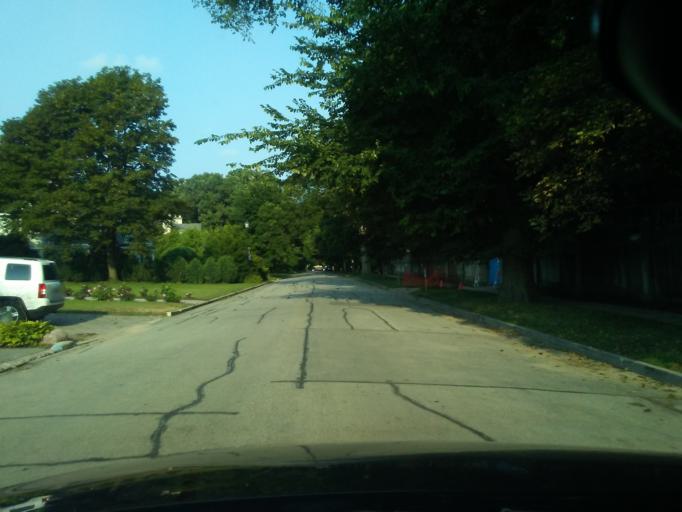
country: US
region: Illinois
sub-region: Cook County
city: Evanston
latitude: 42.0411
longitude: -87.6711
